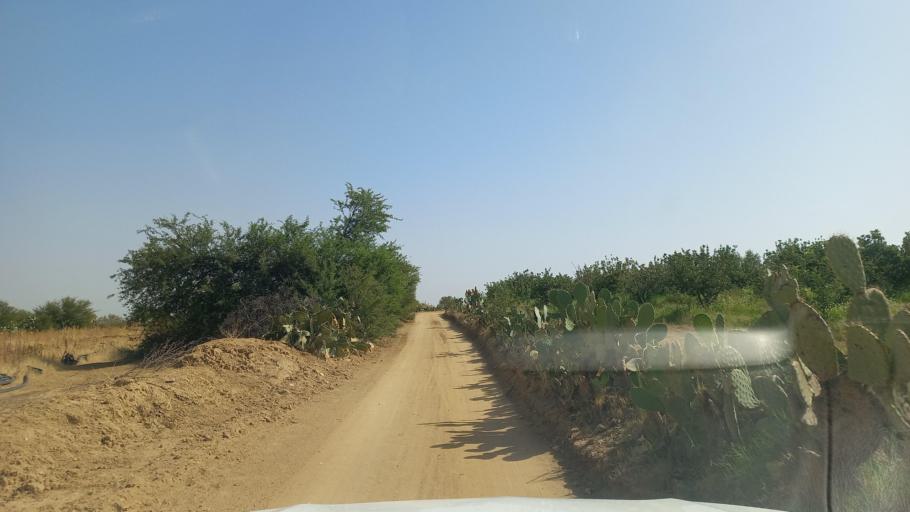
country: TN
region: Al Qasrayn
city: Kasserine
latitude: 35.2453
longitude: 9.0301
